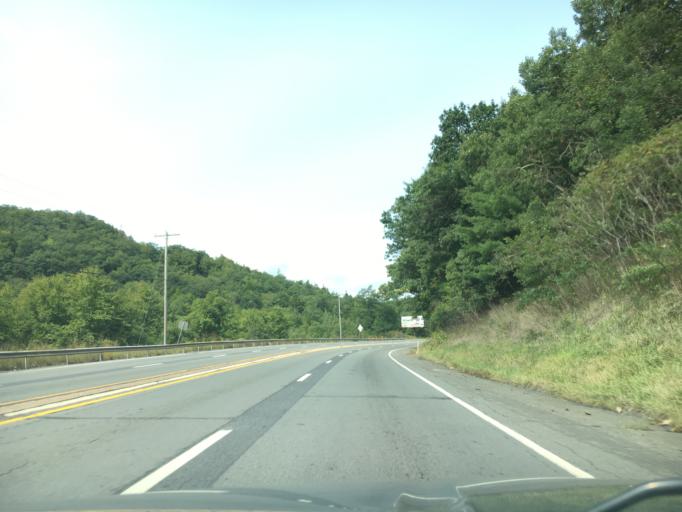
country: US
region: Pennsylvania
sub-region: Schuylkill County
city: Hometown
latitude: 40.8635
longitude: -76.0056
